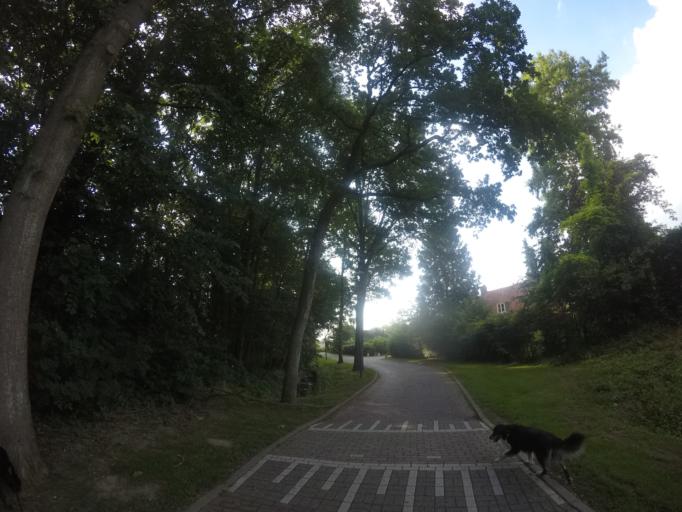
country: NL
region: Gelderland
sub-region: Gemeente Westervoort
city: Westervoort
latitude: 51.9620
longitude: 5.9722
